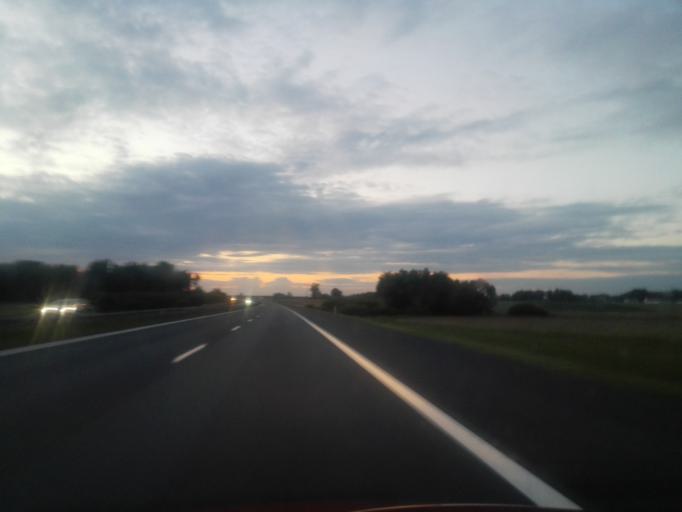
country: PL
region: Lodz Voivodeship
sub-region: Piotrkow Trybunalski
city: Piotrkow Trybunalski
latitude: 51.4488
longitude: 19.6419
